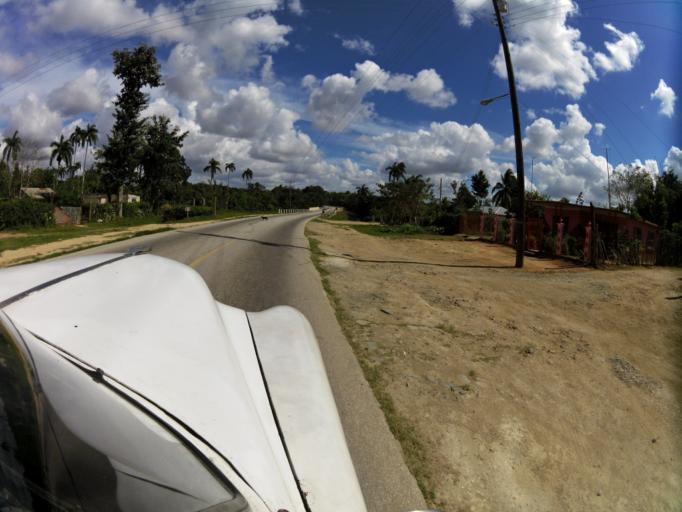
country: CU
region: Holguin
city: Cacocum
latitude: 20.8637
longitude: -76.4412
